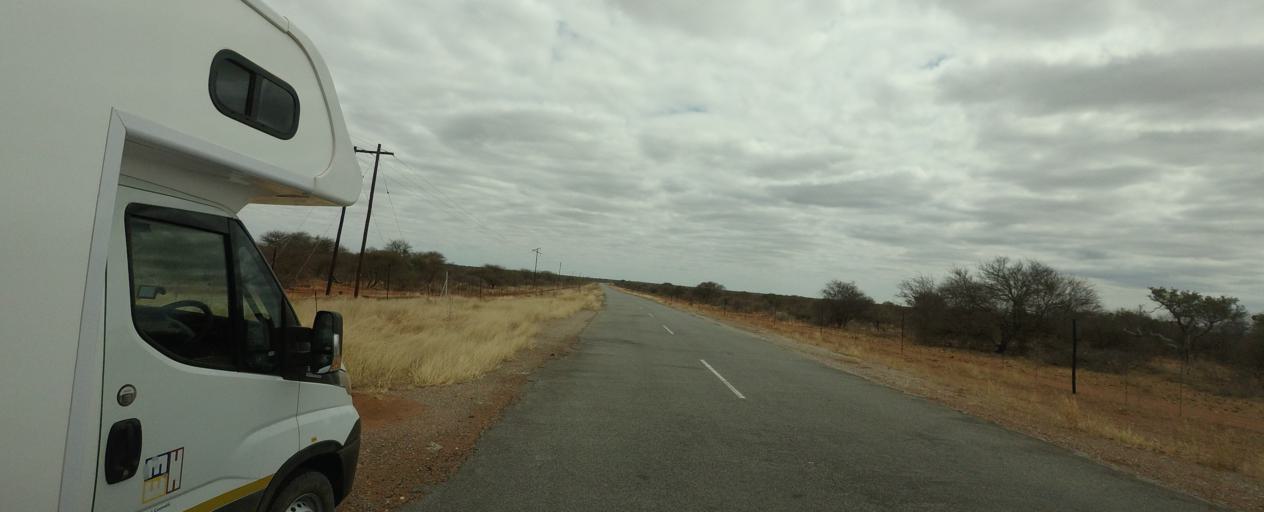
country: BW
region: Central
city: Makobeng
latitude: -22.9993
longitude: 28.1154
